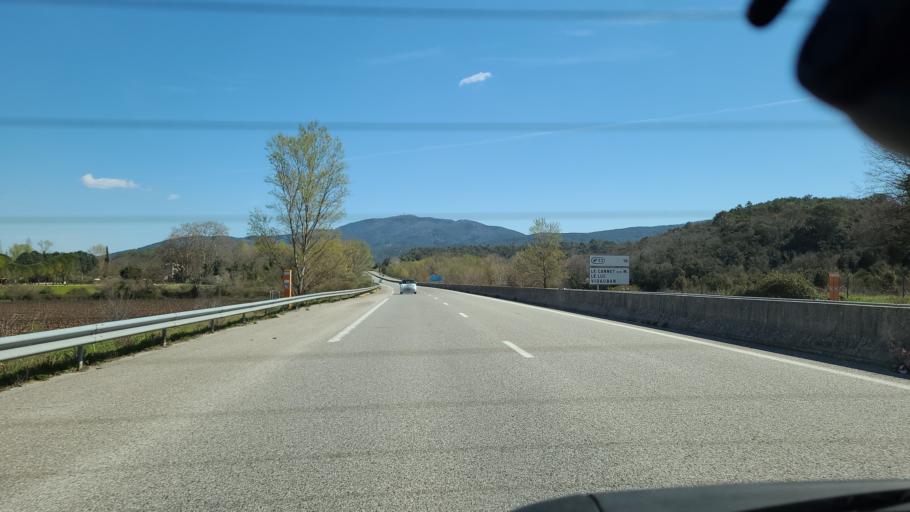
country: FR
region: Provence-Alpes-Cote d'Azur
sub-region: Departement du Var
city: Pignans
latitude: 43.2902
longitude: 6.2085
